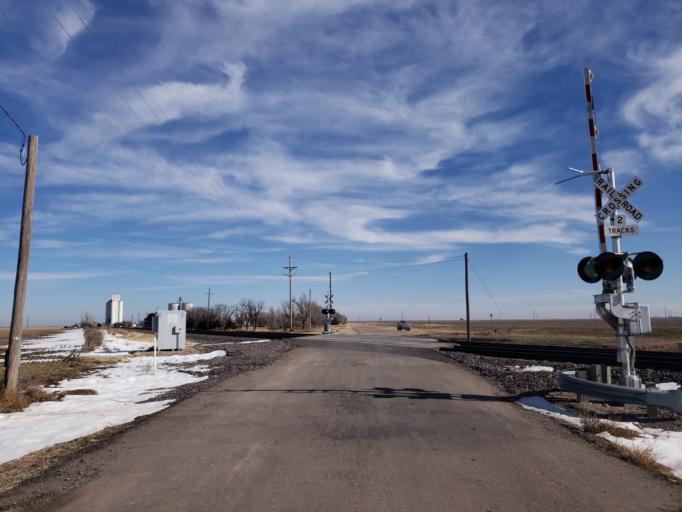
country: US
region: Kansas
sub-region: Ford County
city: Dodge City
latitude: 37.4853
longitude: -99.9052
